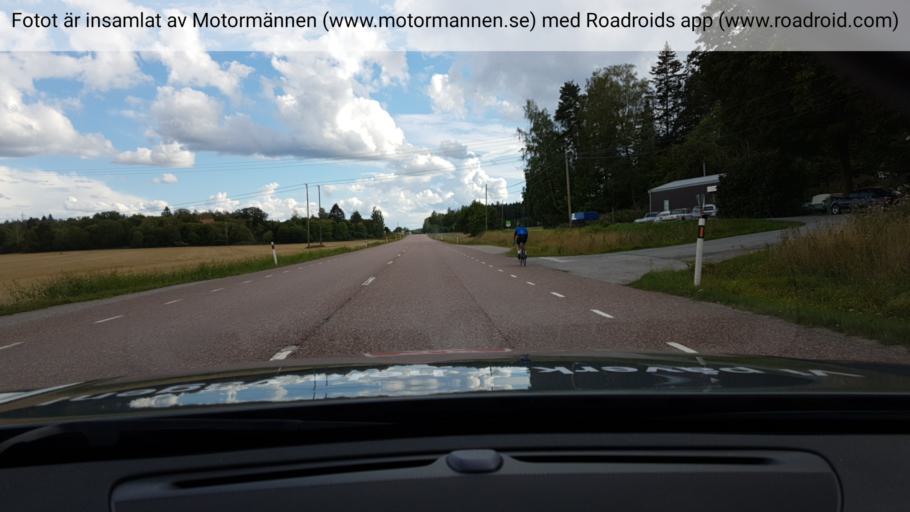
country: SE
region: Soedermanland
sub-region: Strangnas Kommun
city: Strangnas
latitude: 59.3297
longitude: 17.0698
